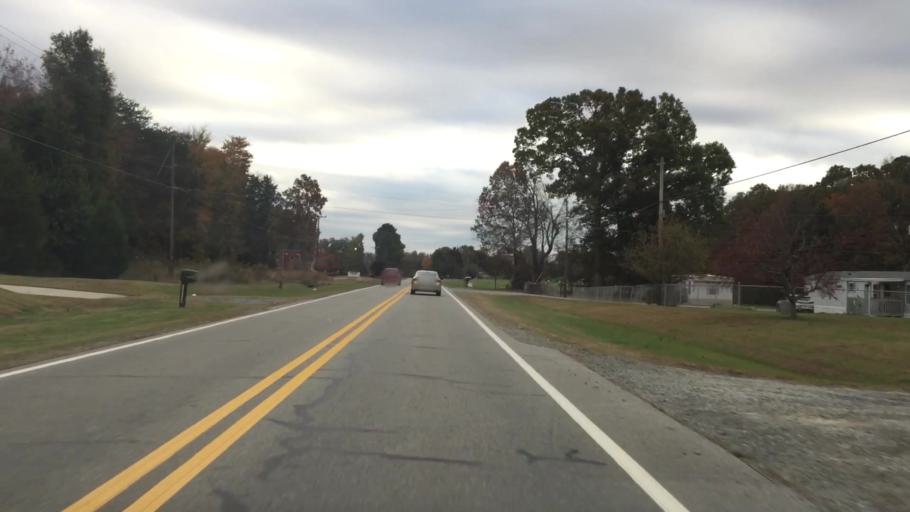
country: US
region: North Carolina
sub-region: Rockingham County
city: Reidsville
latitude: 36.3018
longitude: -79.6208
